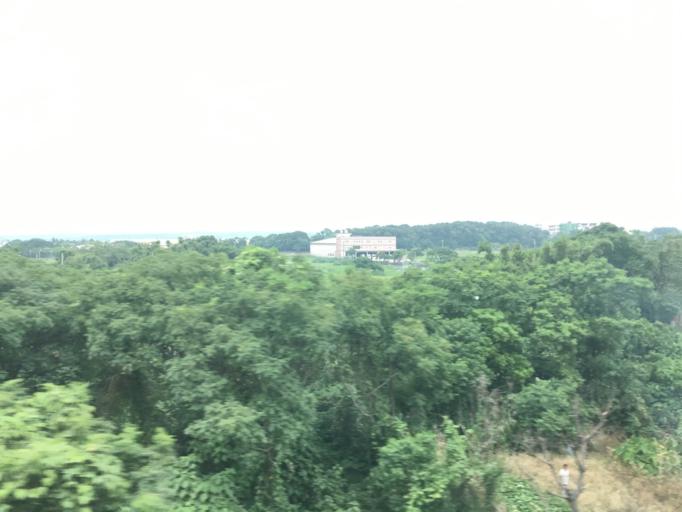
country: TW
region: Taiwan
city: Taoyuan City
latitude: 25.0339
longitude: 121.2165
